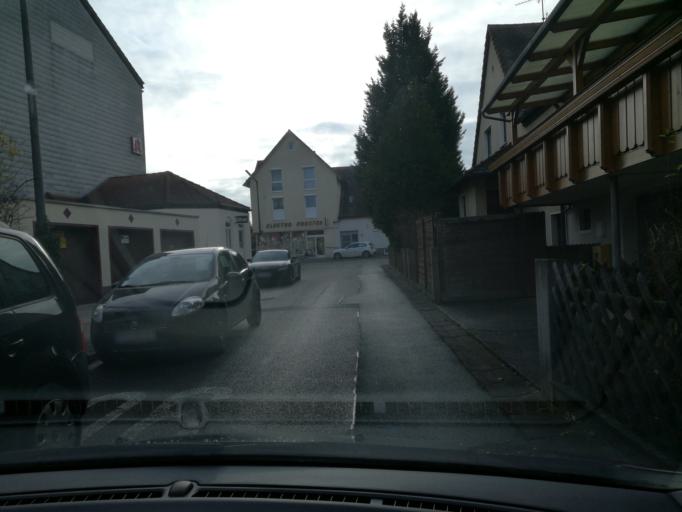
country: DE
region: Bavaria
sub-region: Regierungsbezirk Mittelfranken
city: Veitsbronn
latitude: 49.5083
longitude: 10.8809
